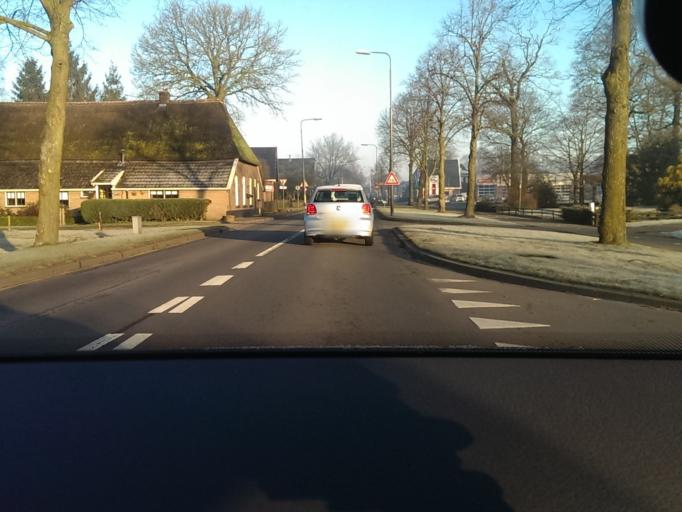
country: NL
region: Overijssel
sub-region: Gemeente Twenterand
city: Vroomshoop
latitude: 52.4297
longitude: 6.5417
